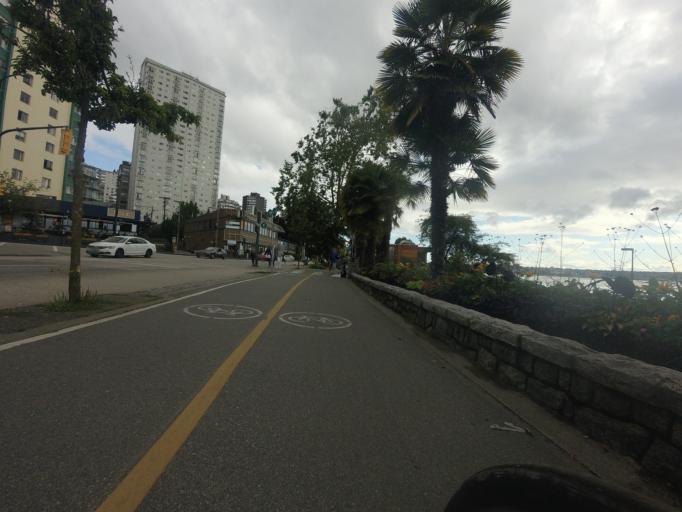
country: CA
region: British Columbia
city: West End
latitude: 49.2872
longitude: -123.1426
